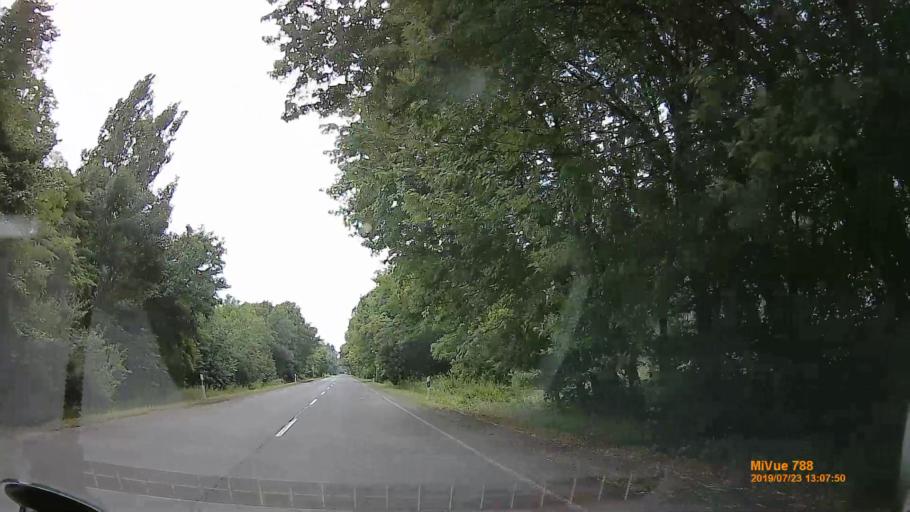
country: HU
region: Szabolcs-Szatmar-Bereg
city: Tiszavasvari
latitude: 47.9522
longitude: 21.3305
